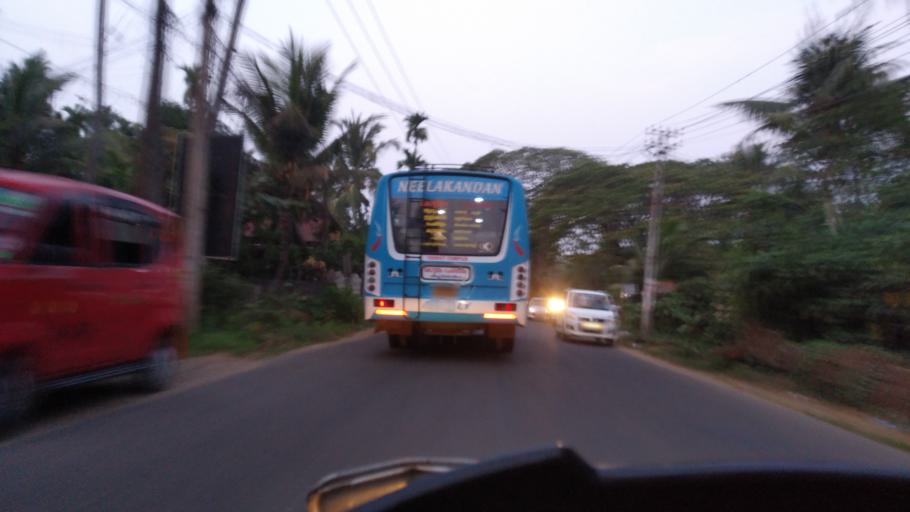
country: IN
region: Kerala
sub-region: Kottayam
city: Kottayam
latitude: 9.5997
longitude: 76.4315
